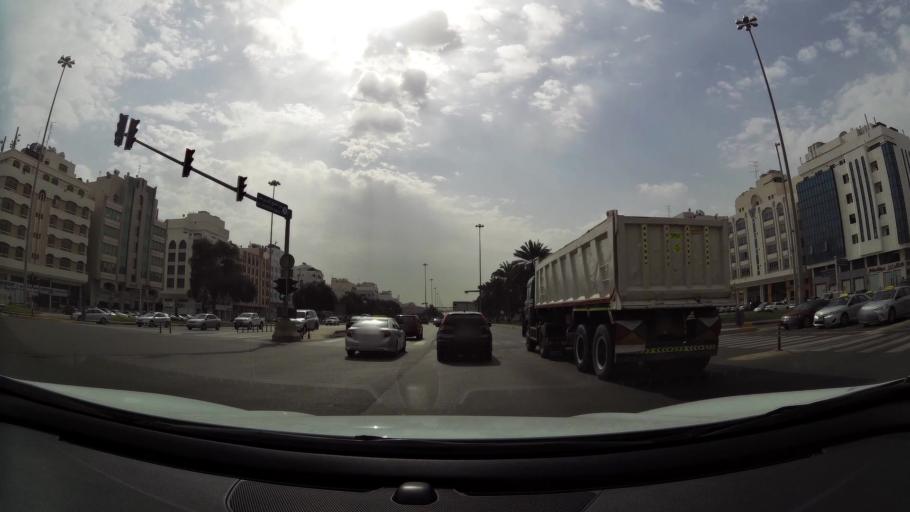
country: AE
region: Abu Dhabi
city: Abu Dhabi
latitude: 24.4577
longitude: 54.3823
